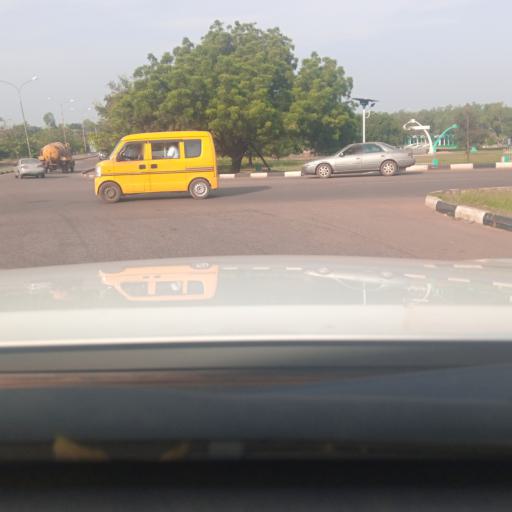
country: NG
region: Enugu
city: Enugu
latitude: 6.4389
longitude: 7.5172
